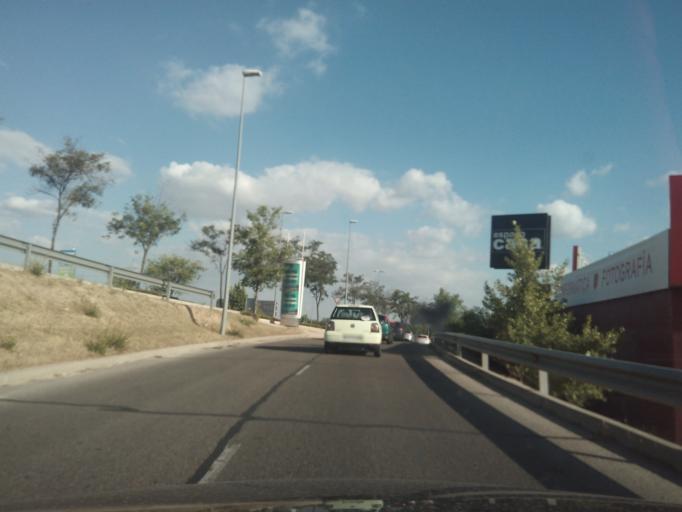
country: ES
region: Madrid
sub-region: Provincia de Madrid
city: San Sebastian de los Reyes
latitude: 40.5459
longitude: -3.6101
